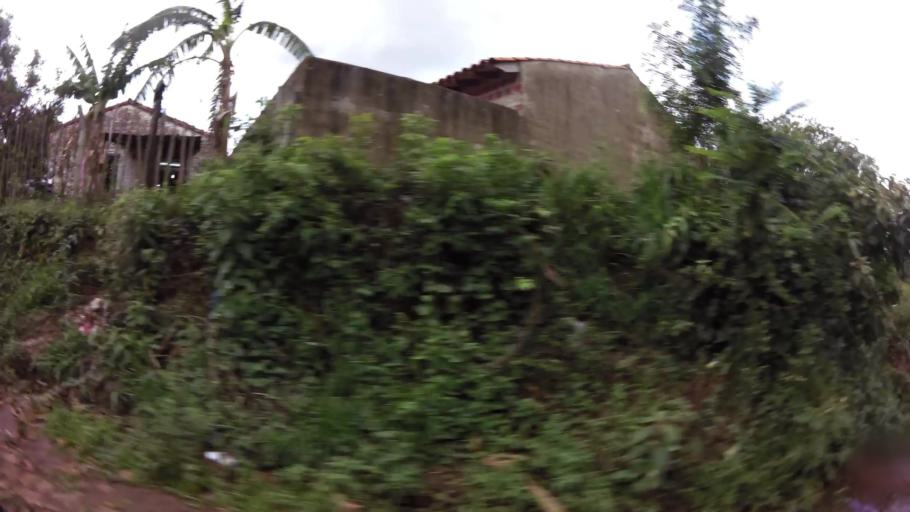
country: PY
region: Central
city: San Lorenzo
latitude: -25.2873
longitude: -57.4924
